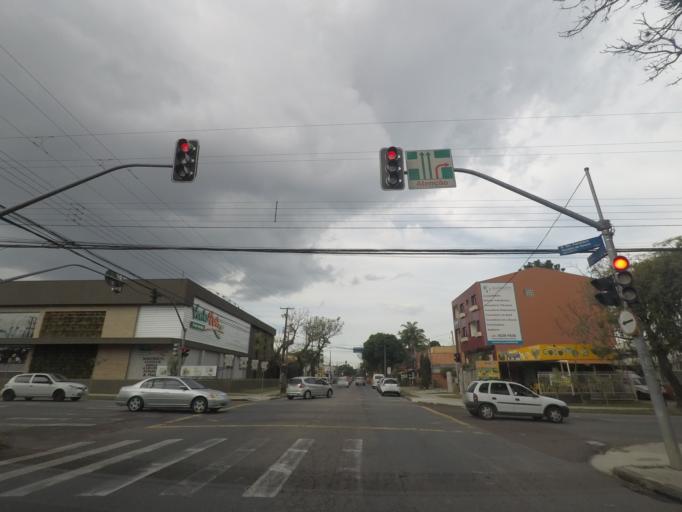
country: BR
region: Parana
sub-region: Curitiba
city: Curitiba
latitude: -25.4815
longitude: -49.2488
